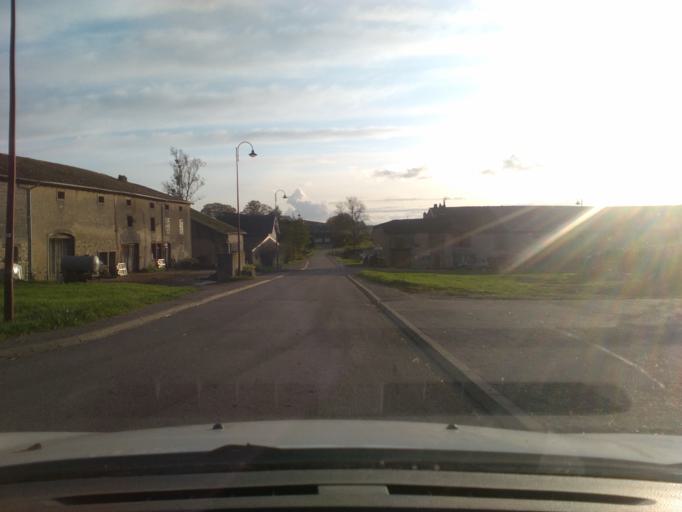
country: FR
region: Lorraine
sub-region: Departement des Vosges
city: Mirecourt
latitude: 48.2498
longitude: 6.1570
